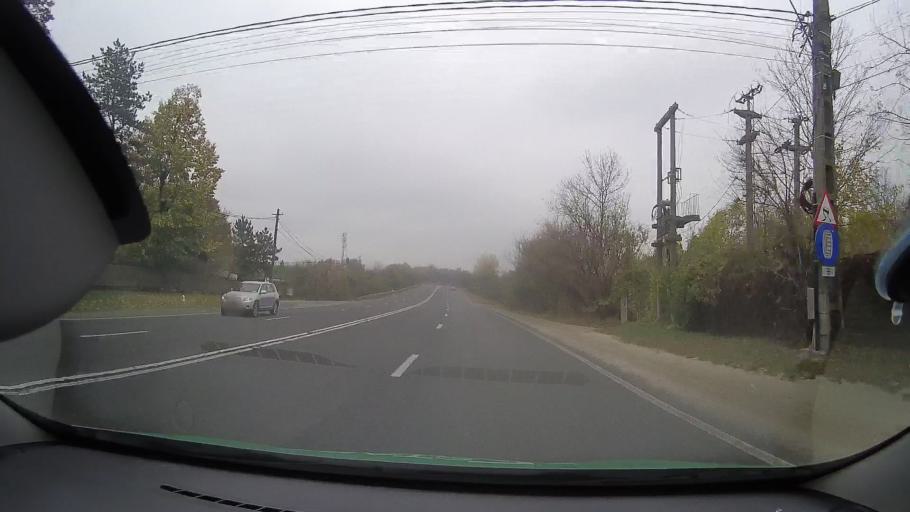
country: RO
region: Ilfov
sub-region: Comuna Ciolpani
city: Ciolpani
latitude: 44.7435
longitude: 26.1107
